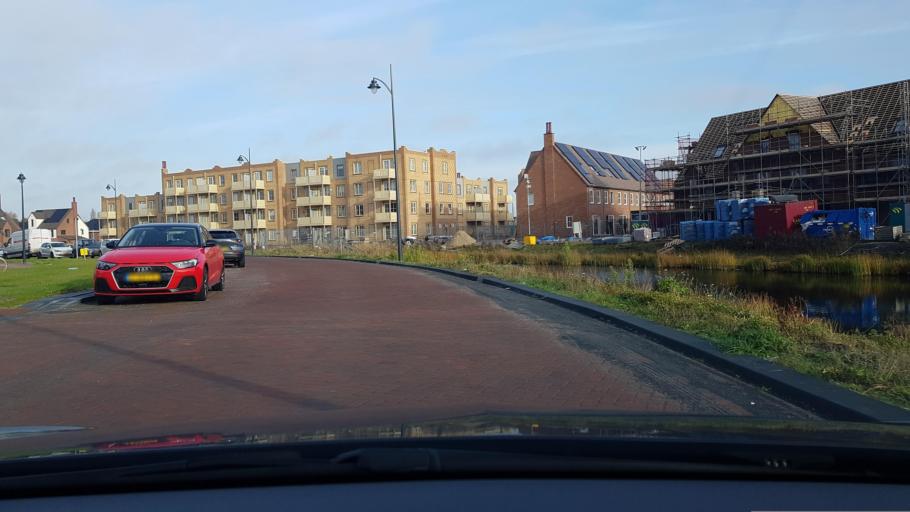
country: NL
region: North Holland
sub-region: Gemeente Haarlemmermeer
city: Hoofddorp
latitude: 52.2888
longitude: 4.6623
